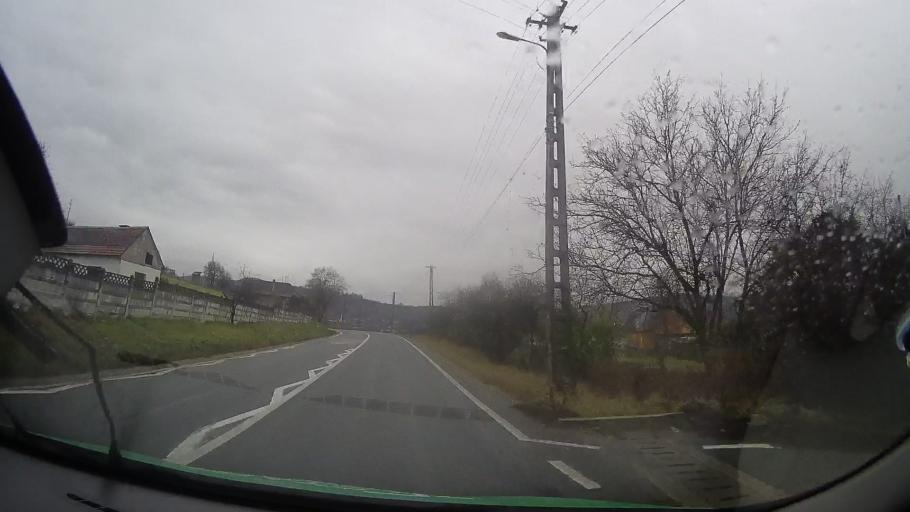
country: RO
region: Bistrita-Nasaud
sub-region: Comuna Teaca
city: Teaca
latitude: 46.9153
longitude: 24.4961
